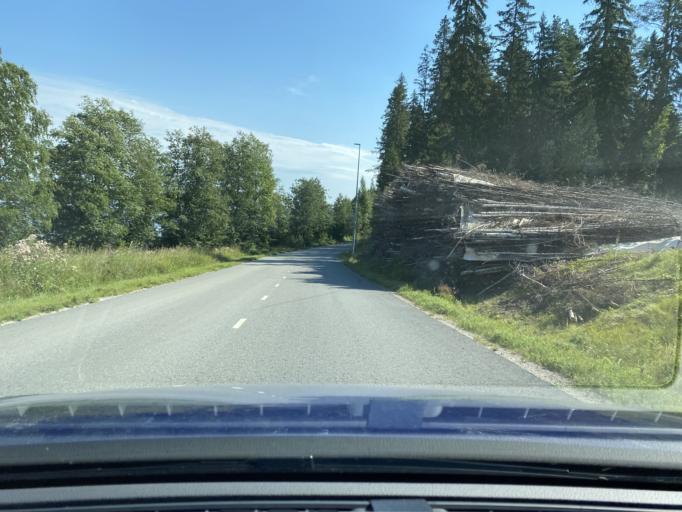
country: FI
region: Central Finland
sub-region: Jyvaeskylae
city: Korpilahti
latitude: 61.8893
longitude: 25.3952
